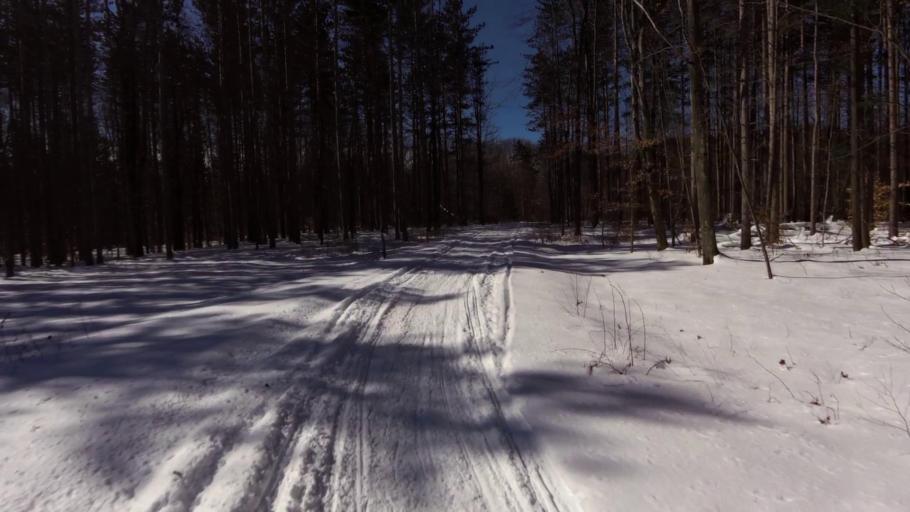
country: US
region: New York
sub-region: Allegany County
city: Cuba
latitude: 42.3001
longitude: -78.2409
